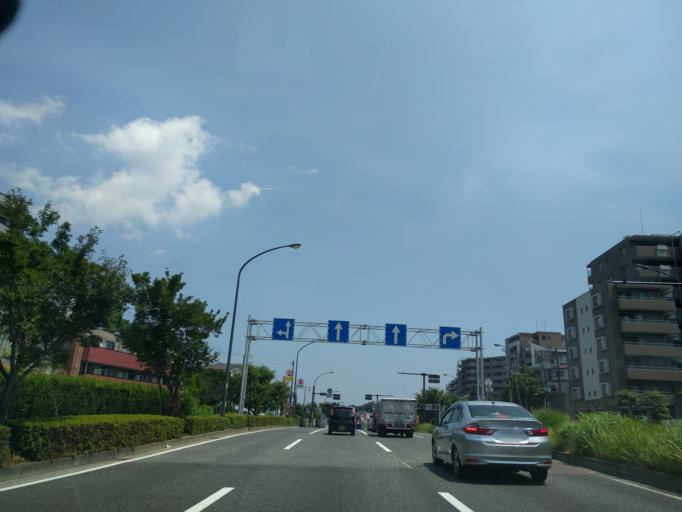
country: JP
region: Kanagawa
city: Yokohama
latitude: 35.4008
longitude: 139.5775
